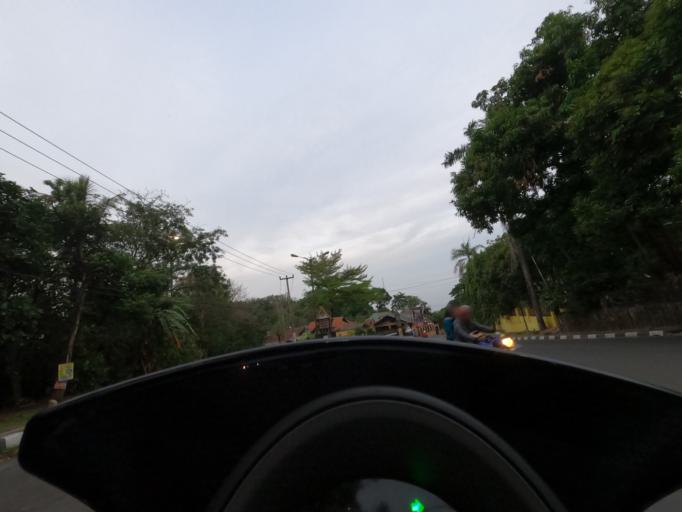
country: ID
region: West Java
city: Lembang
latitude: -6.5784
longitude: 107.7520
